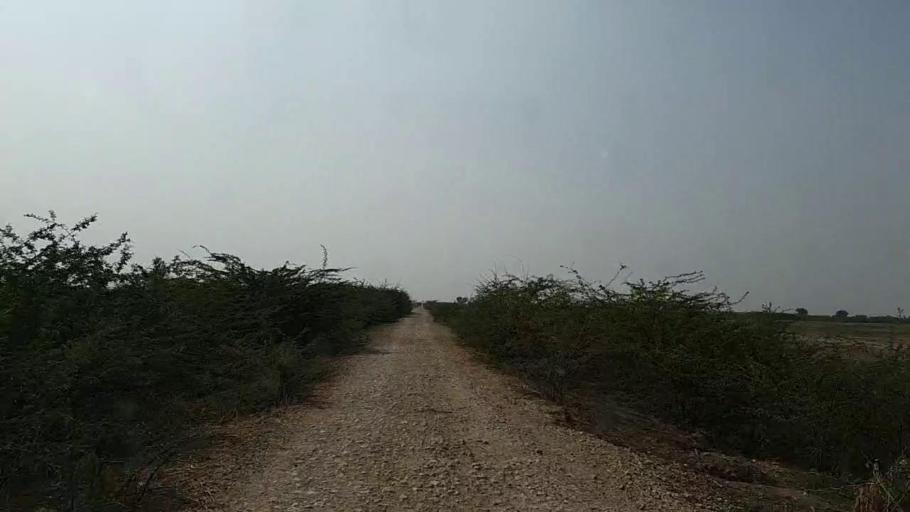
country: PK
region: Sindh
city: Naukot
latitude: 24.7606
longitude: 69.3157
